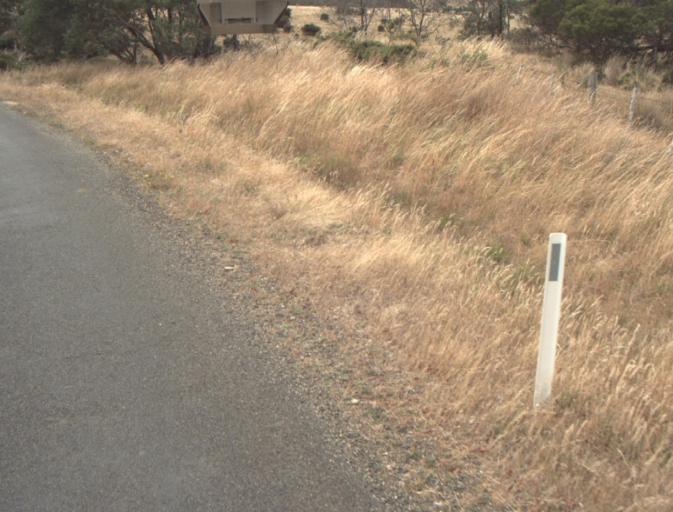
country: AU
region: Tasmania
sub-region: Northern Midlands
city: Evandale
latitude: -41.5081
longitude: 147.3647
